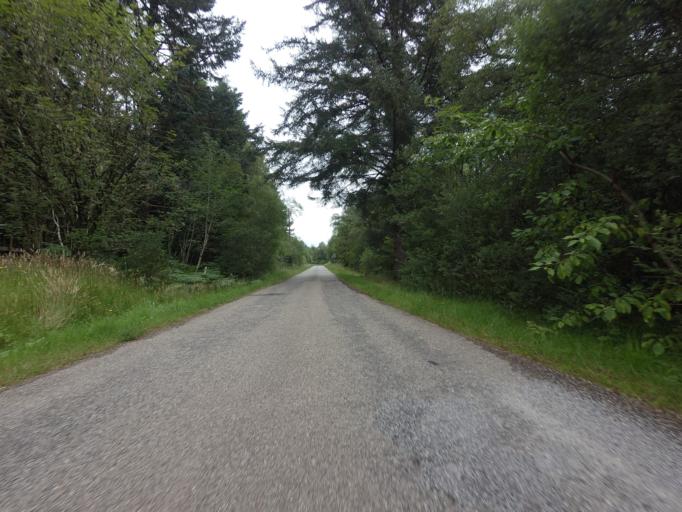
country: GB
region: Scotland
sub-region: Highland
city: Evanton
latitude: 57.9677
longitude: -4.4118
